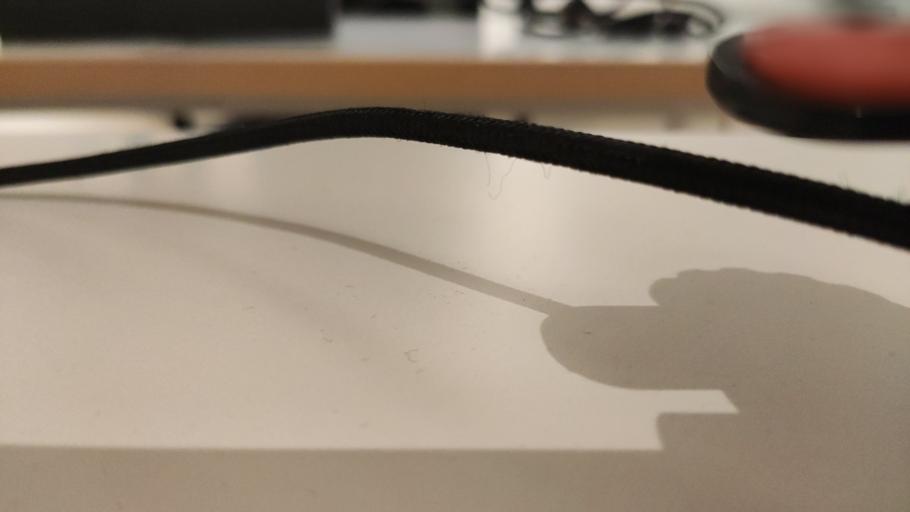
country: RU
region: Moskovskaya
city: Dorokhovo
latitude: 55.5031
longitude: 36.3461
